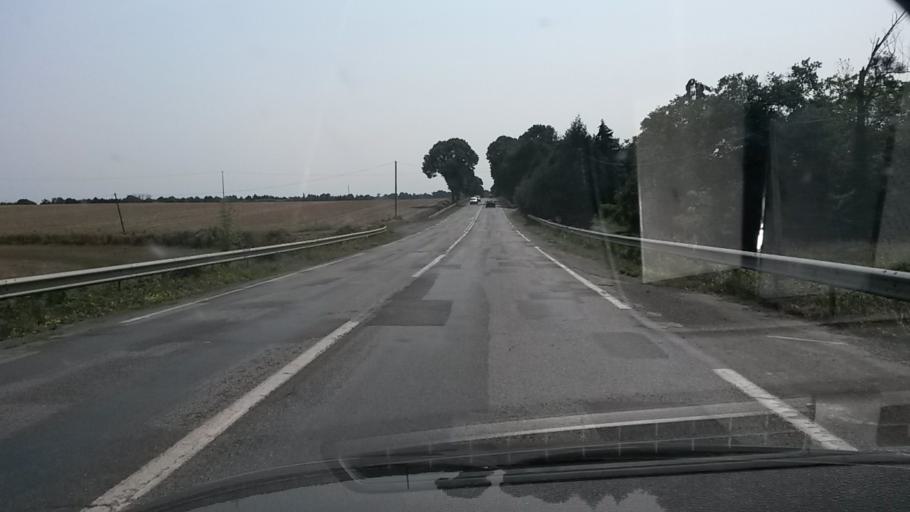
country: FR
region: Pays de la Loire
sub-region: Departement de la Mayenne
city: Chateau-Gontier
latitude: 47.9067
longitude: -0.6859
